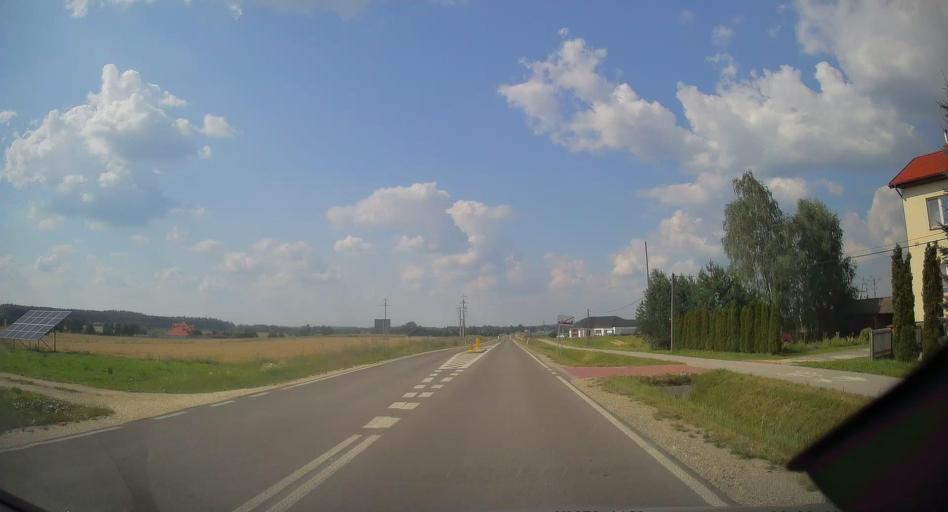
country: PL
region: Swietokrzyskie
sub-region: Powiat kielecki
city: Lopuszno
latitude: 50.9554
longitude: 20.2504
